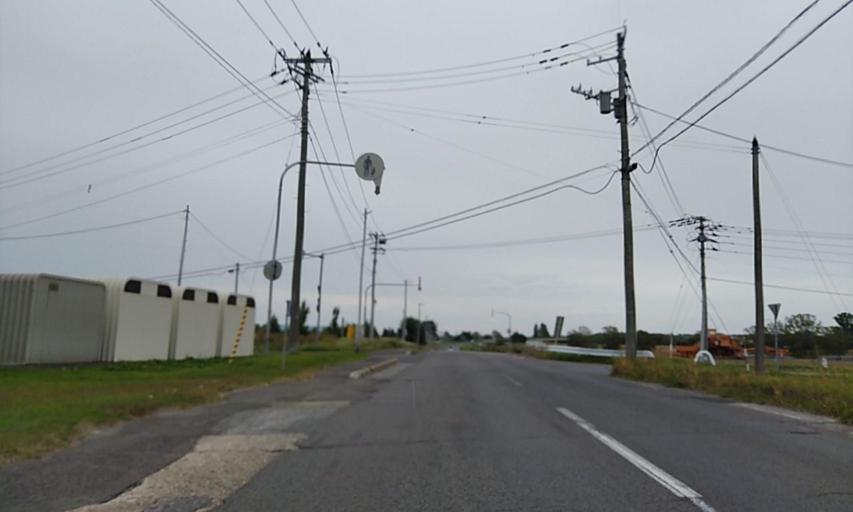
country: JP
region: Hokkaido
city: Bihoro
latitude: 43.8351
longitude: 144.1101
